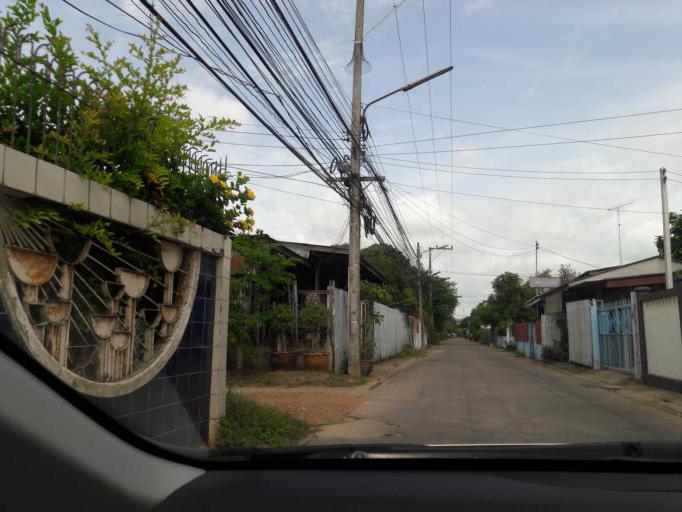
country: TH
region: Ratchaburi
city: Ratchaburi
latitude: 13.5342
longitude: 99.8324
